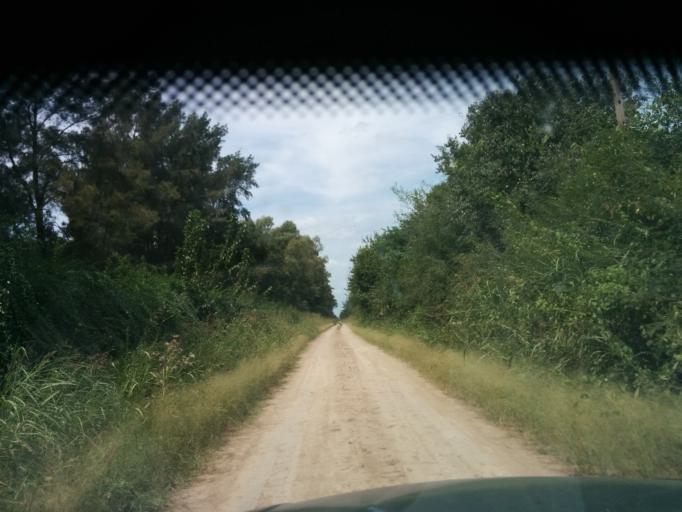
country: AR
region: Buenos Aires
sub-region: Partido de Campana
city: Campana
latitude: -34.2838
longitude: -58.9535
